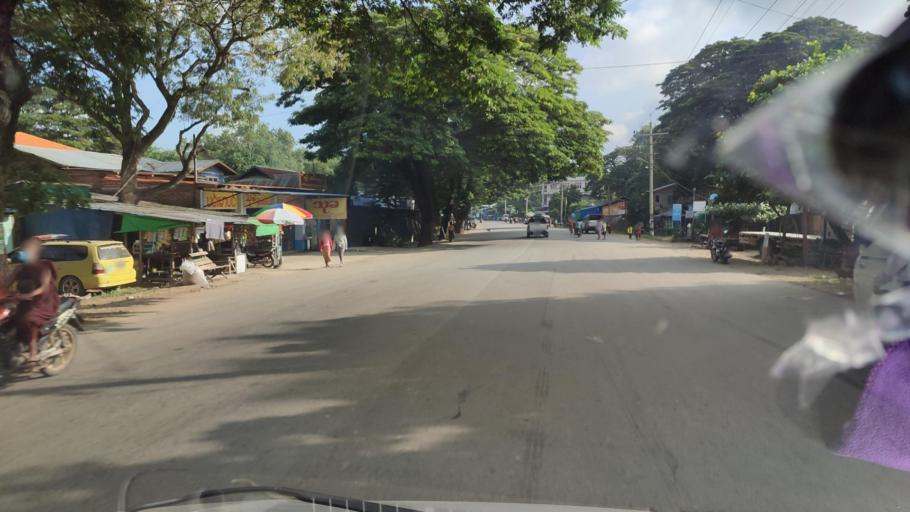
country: MM
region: Mandalay
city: Yamethin
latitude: 20.7574
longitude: 96.3145
